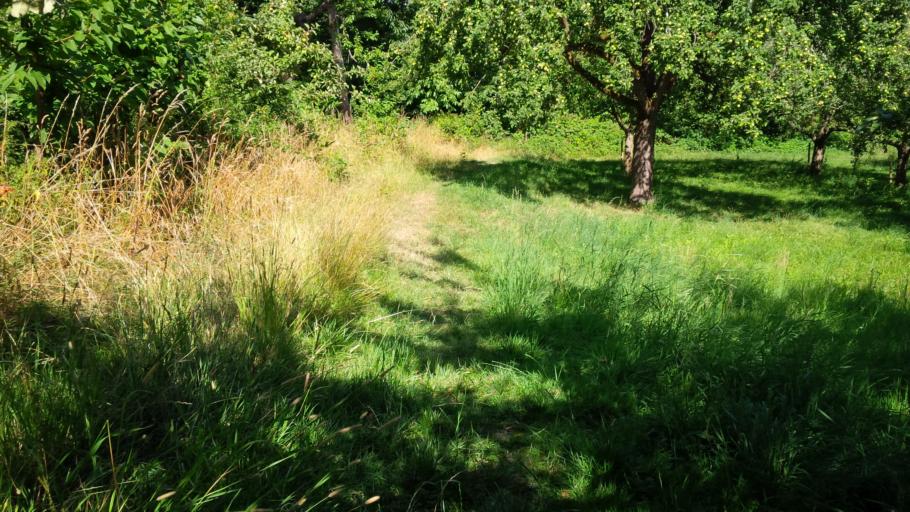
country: DE
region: Hesse
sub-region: Regierungsbezirk Darmstadt
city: Bad Soden am Taunus
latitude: 50.1588
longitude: 8.4975
